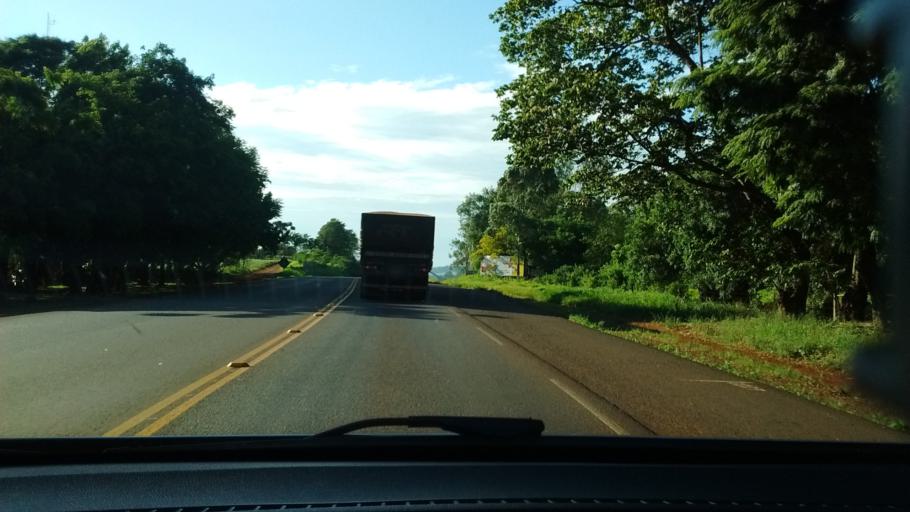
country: BR
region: Parana
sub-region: Cascavel
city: Cascavel
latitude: -25.2502
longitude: -53.5788
